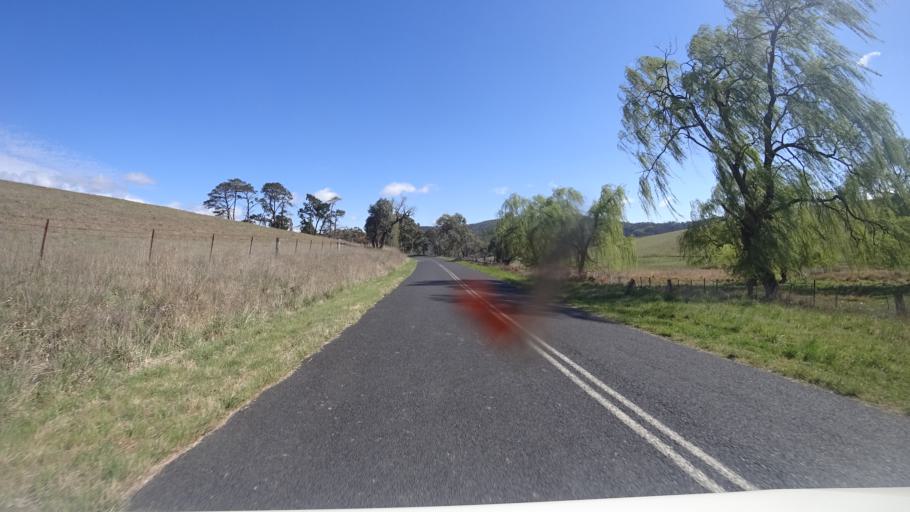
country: AU
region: New South Wales
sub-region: Lithgow
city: Bowenfels
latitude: -33.5181
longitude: 149.9596
